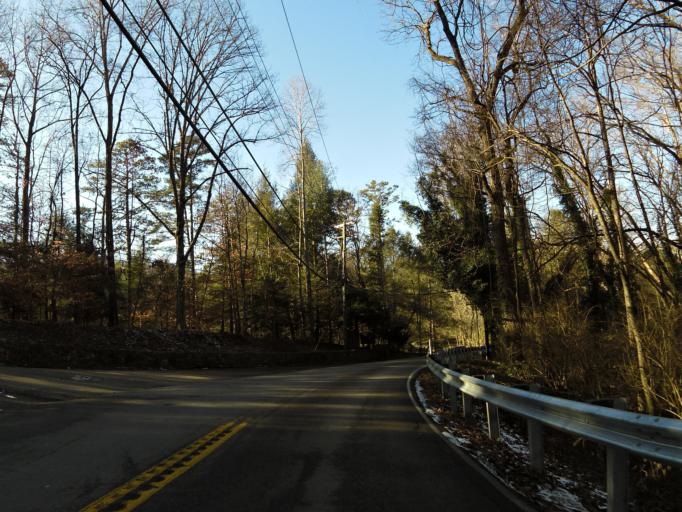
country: US
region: Tennessee
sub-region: Knox County
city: Knoxville
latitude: 35.9117
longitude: -83.9856
